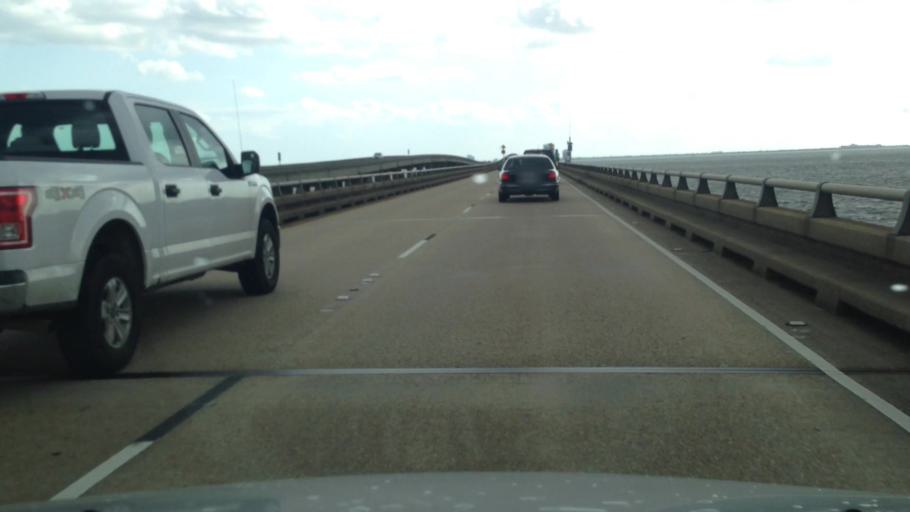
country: US
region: Louisiana
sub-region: Jefferson Parish
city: Metairie
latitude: 30.0805
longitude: -90.1438
